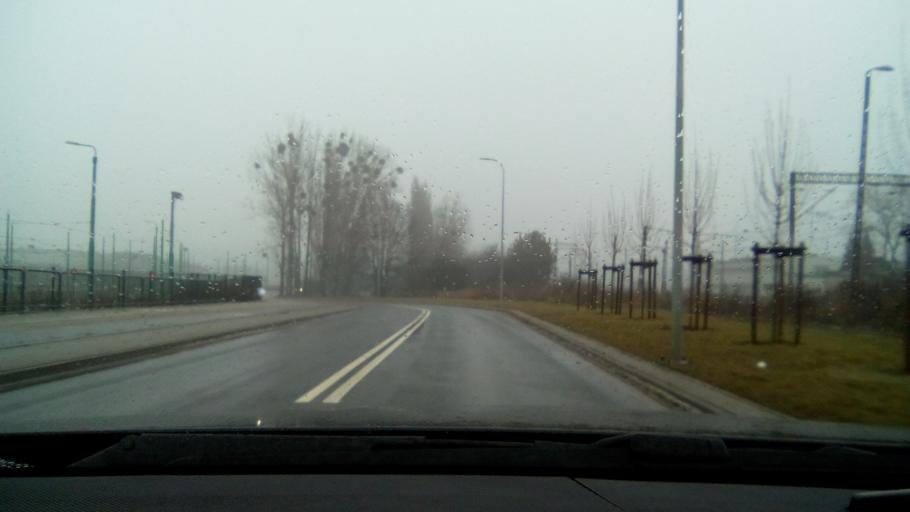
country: PL
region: Greater Poland Voivodeship
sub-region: Poznan
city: Poznan
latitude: 52.3819
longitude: 17.0045
